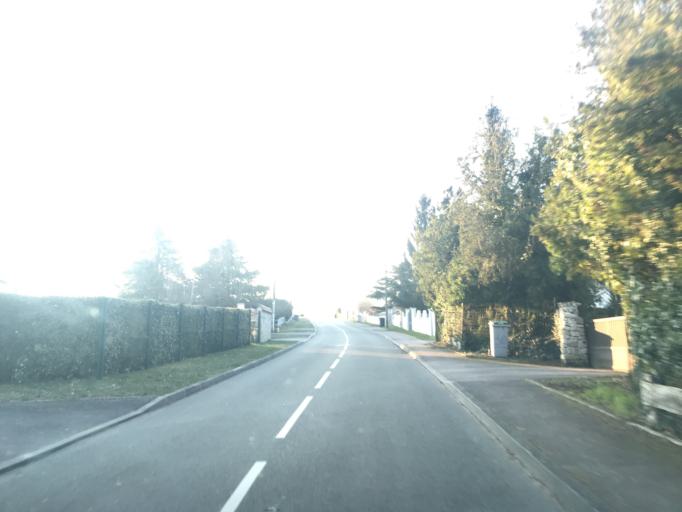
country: FR
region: Haute-Normandie
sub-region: Departement de l'Eure
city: Gasny
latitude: 49.0727
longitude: 1.5969
